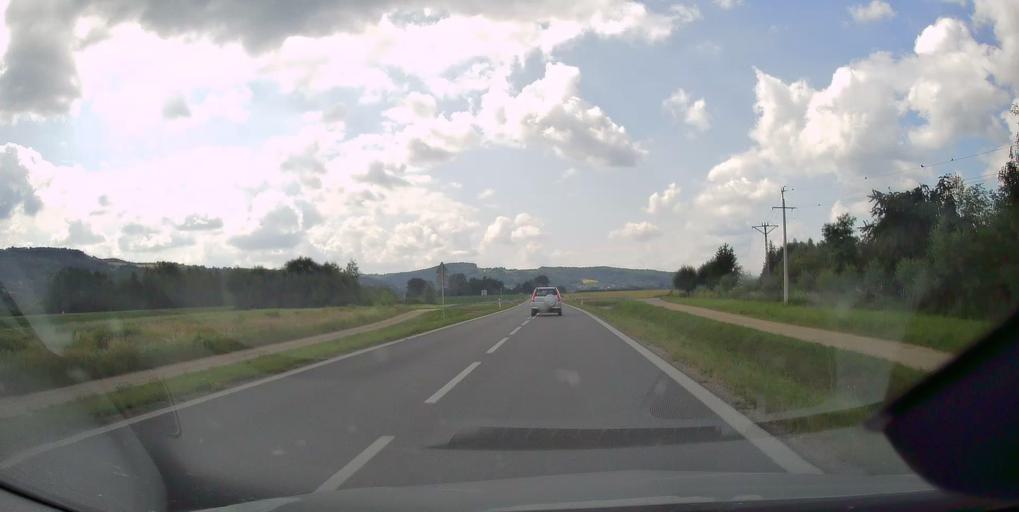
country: PL
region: Lesser Poland Voivodeship
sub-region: Powiat tarnowski
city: Wojnicz
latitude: 49.9376
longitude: 20.8445
